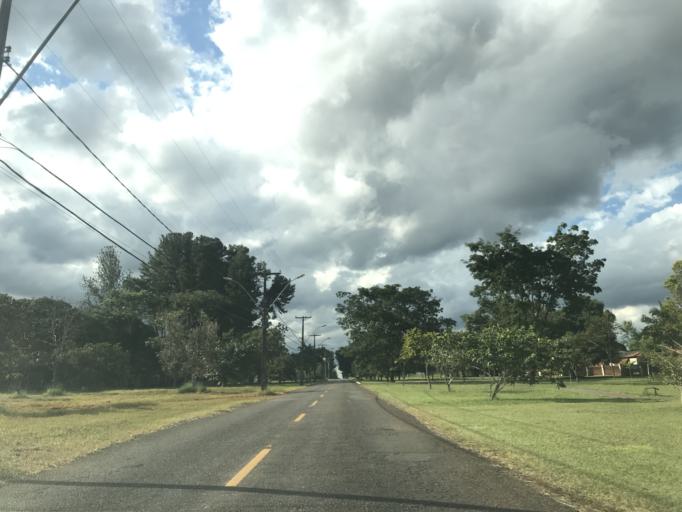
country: BR
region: Federal District
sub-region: Brasilia
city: Brasilia
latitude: -15.9106
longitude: -47.9411
